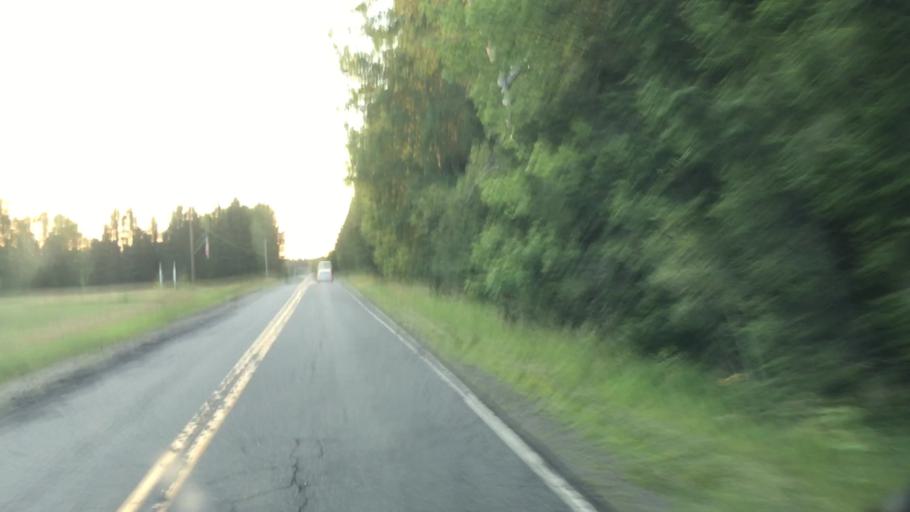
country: US
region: Maine
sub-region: Penobscot County
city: Medway
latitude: 45.5987
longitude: -68.2466
